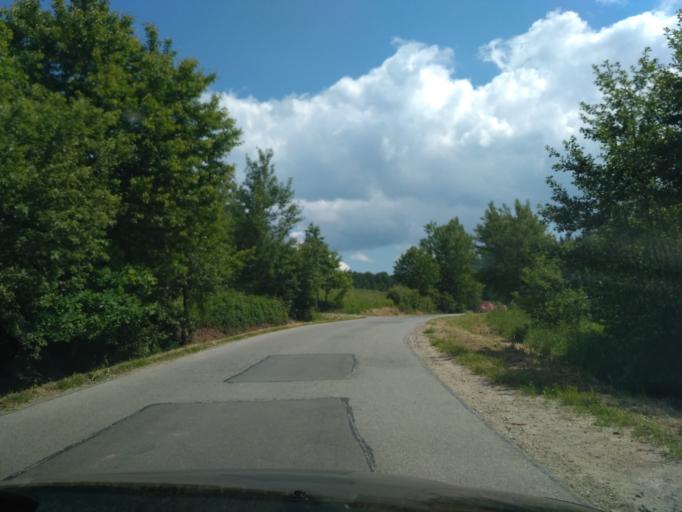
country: PL
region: Subcarpathian Voivodeship
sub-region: Powiat brzozowski
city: Wesola
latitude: 49.8337
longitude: 22.0638
